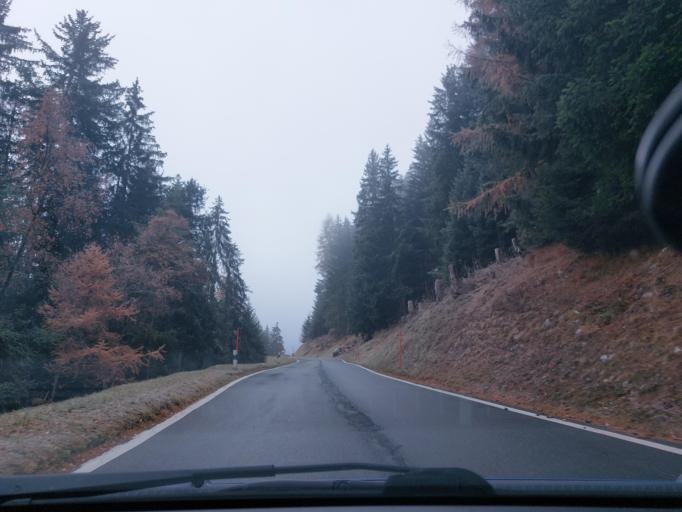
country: CH
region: Valais
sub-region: Conthey District
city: Basse-Nendaz
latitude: 46.1616
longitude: 7.3124
